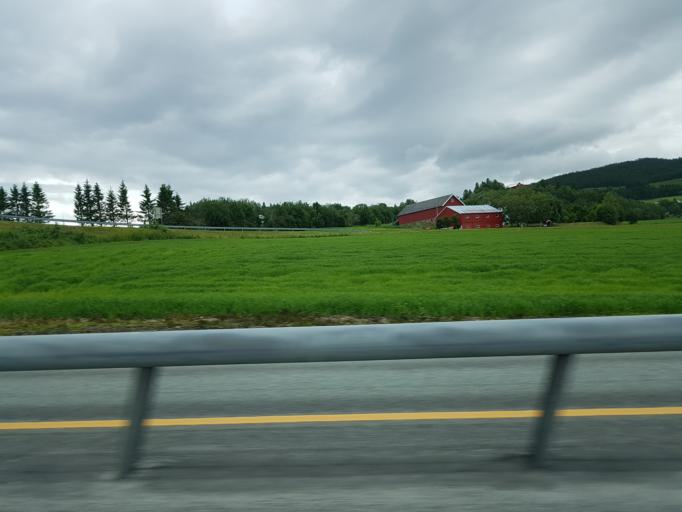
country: NO
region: Nord-Trondelag
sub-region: Stjordal
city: Stjordal
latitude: 63.5274
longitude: 10.8386
